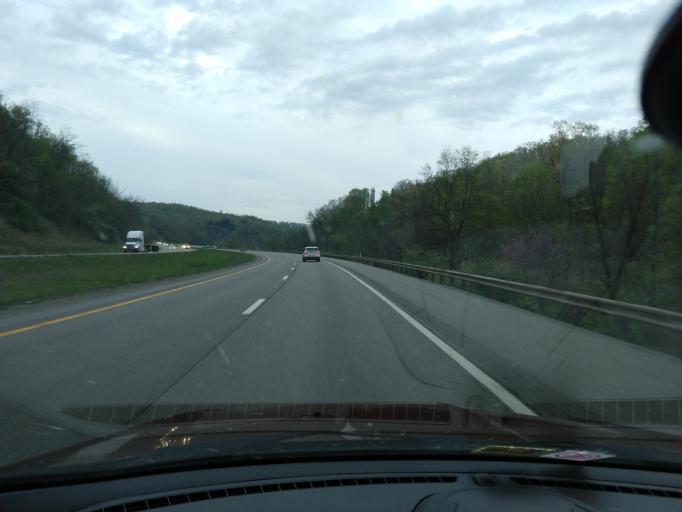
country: US
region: West Virginia
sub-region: Lewis County
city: Weston
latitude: 39.0644
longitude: -80.4022
